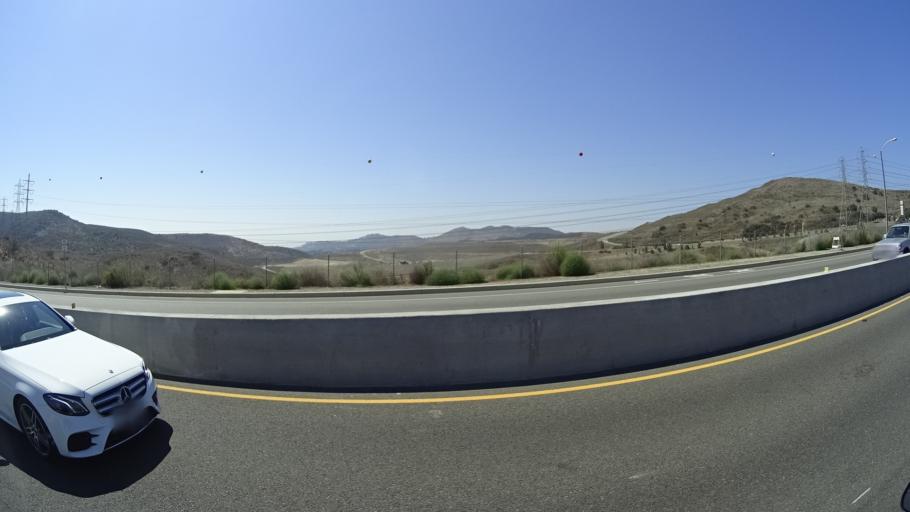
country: US
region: California
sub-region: Orange County
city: San Juan Capistrano
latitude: 33.4900
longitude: -117.6125
